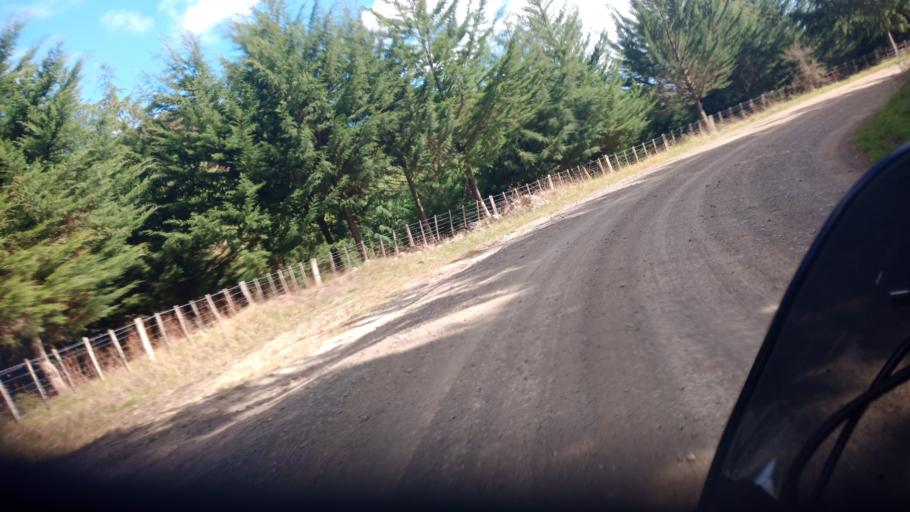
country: NZ
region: Gisborne
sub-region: Gisborne District
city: Gisborne
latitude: -38.4204
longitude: 177.7035
